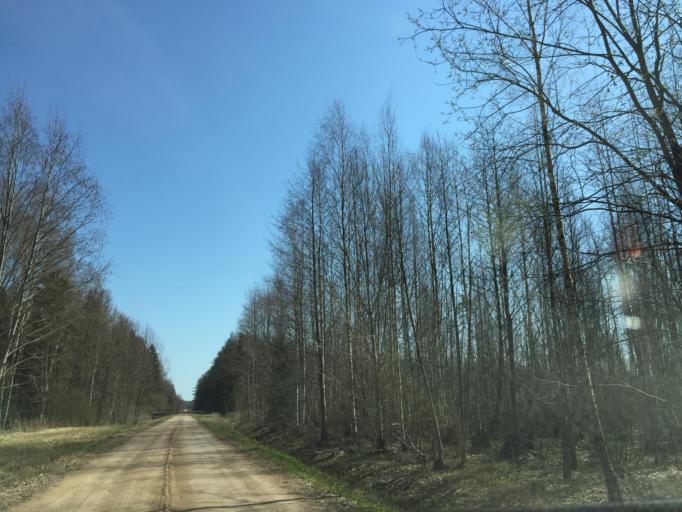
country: EE
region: Tartu
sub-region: Tartu linn
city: Tartu
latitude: 58.5285
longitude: 26.8989
